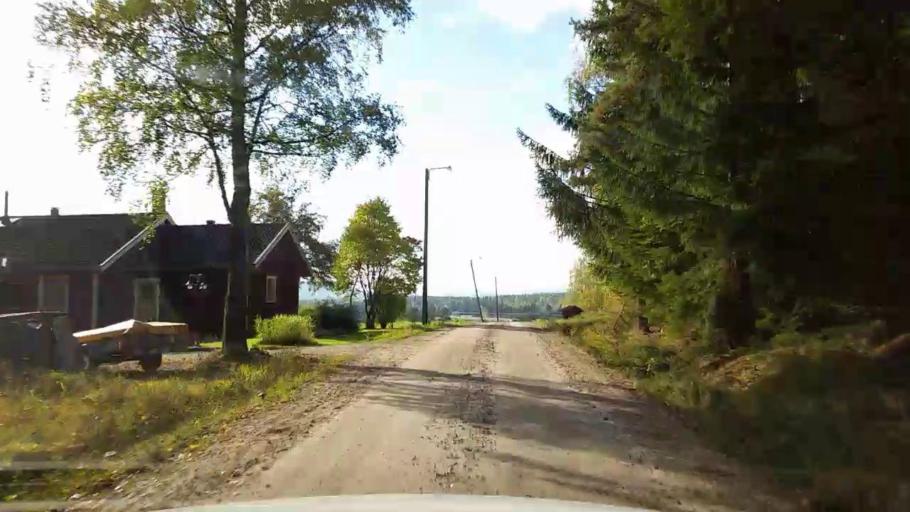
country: SE
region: Gaevleborg
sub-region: Ljusdals Kommun
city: Jaervsoe
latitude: 61.7854
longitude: 16.1660
